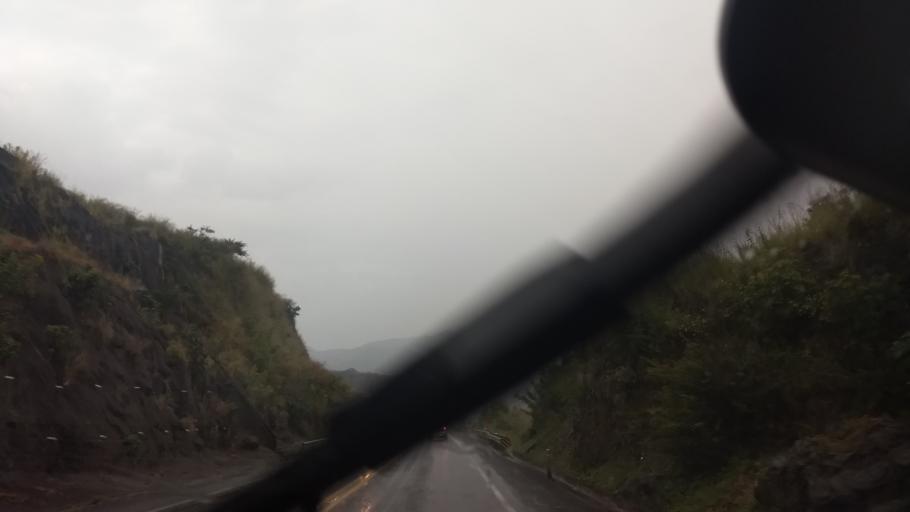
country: MX
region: Jalisco
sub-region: Tonila
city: San Marcos
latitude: 19.4395
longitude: -103.4769
